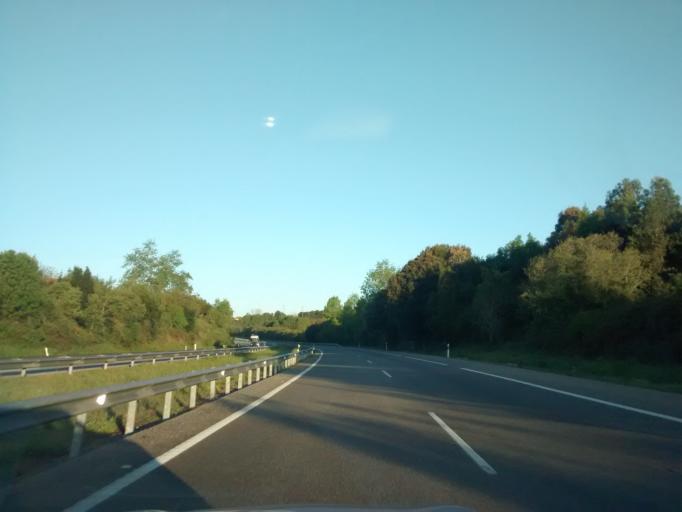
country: ES
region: Asturias
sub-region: Province of Asturias
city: Ribadesella
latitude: 43.4452
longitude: -4.9176
